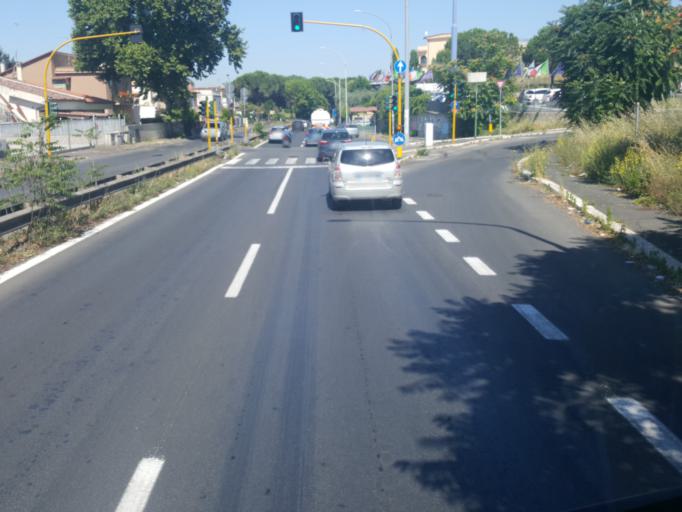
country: IT
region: Latium
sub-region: Citta metropolitana di Roma Capitale
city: Ciampino
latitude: 41.8273
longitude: 12.6255
